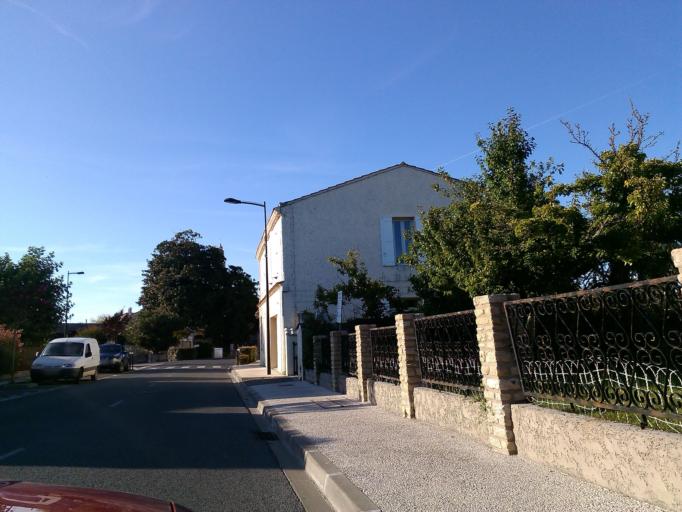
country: FR
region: Aquitaine
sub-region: Departement de la Gironde
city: Soulac-sur-Mer
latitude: 45.4289
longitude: -1.0349
